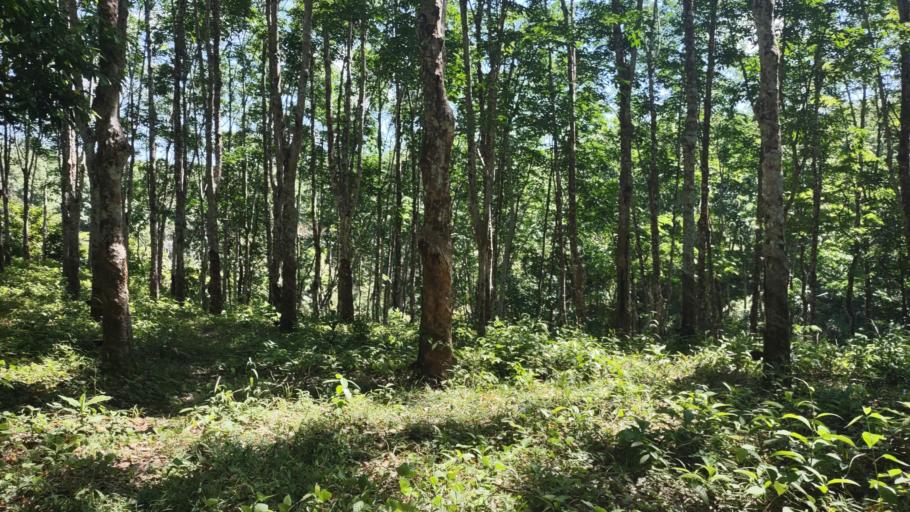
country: MX
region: Veracruz
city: Las Choapas
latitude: 17.7716
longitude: -94.1488
